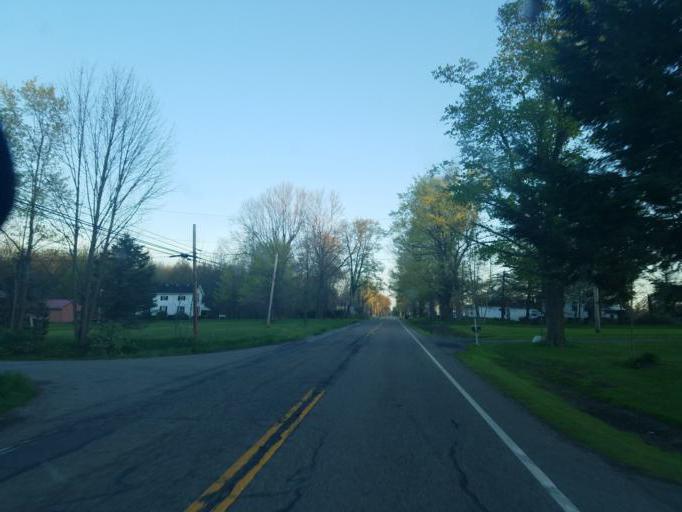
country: US
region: Ohio
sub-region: Trumbull County
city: Brookfield Center
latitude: 41.3680
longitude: -80.5689
